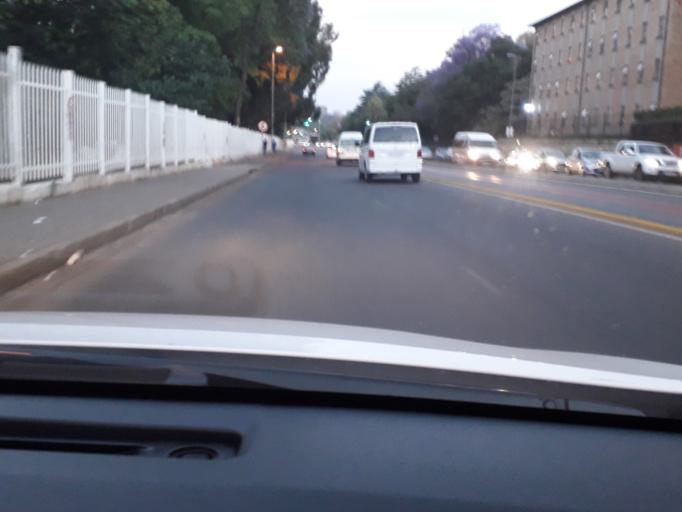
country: ZA
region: Gauteng
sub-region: City of Johannesburg Metropolitan Municipality
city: Johannesburg
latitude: -26.1836
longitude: 28.0065
